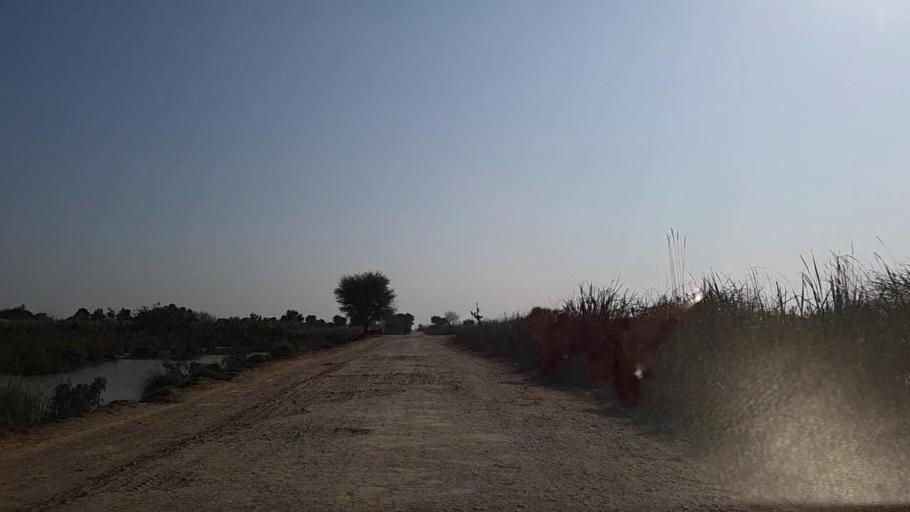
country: PK
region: Sindh
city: Tando Mittha Khan
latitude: 25.9014
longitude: 69.0771
